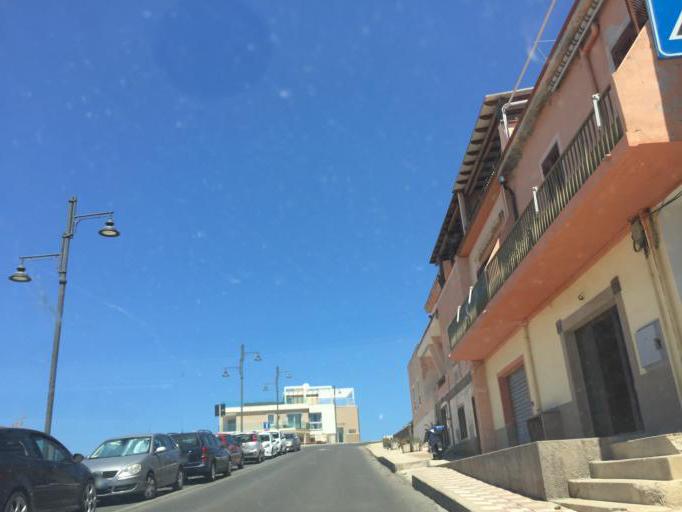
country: IT
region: Sardinia
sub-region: Provincia di Sassari
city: Castelsardo
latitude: 40.9152
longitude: 8.7112
